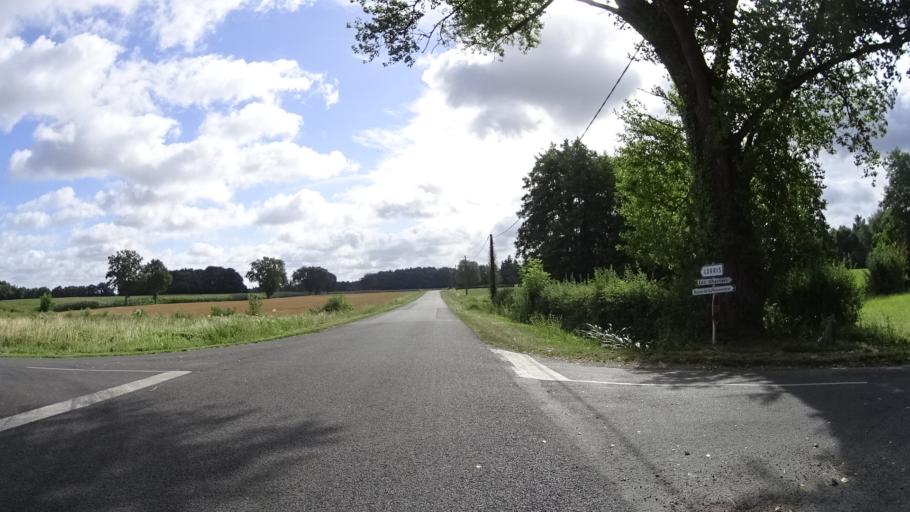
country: FR
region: Centre
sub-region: Departement du Loiret
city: Lorris
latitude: 47.8931
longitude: 2.4781
